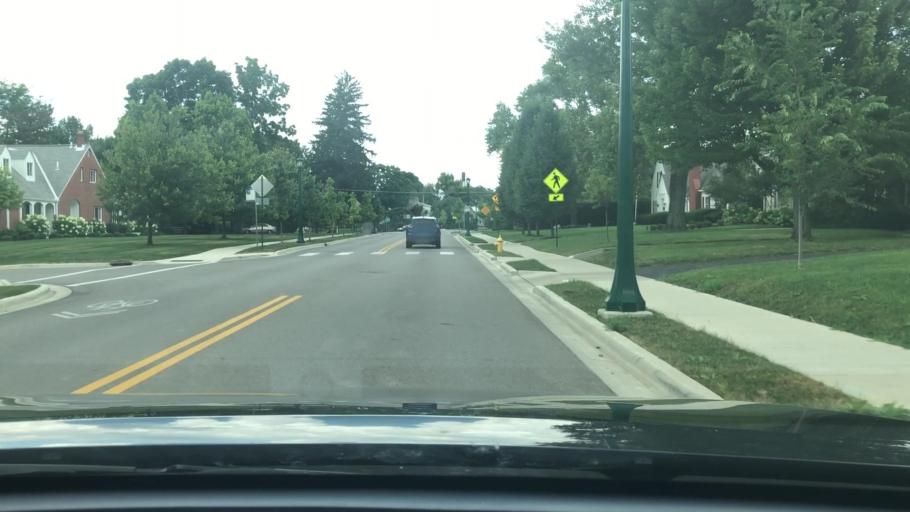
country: US
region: Ohio
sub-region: Franklin County
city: Upper Arlington
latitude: 40.0093
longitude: -83.0699
